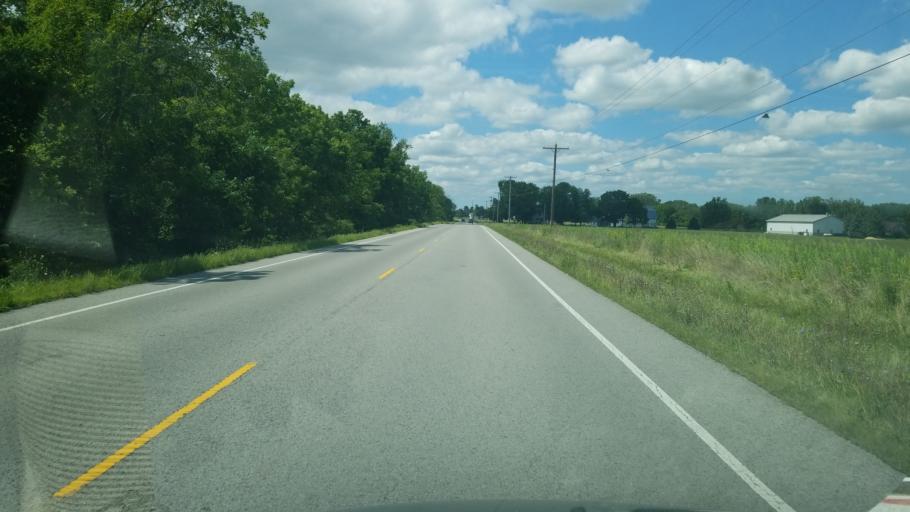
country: US
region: Ohio
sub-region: Henry County
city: Liberty Center
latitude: 41.4127
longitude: -84.0150
